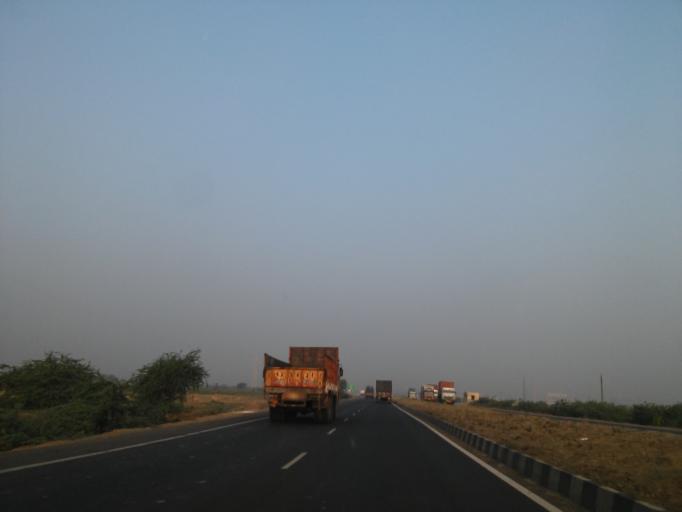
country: IN
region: Gujarat
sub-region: Kachchh
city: Bhachau
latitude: 23.2546
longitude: 70.6506
